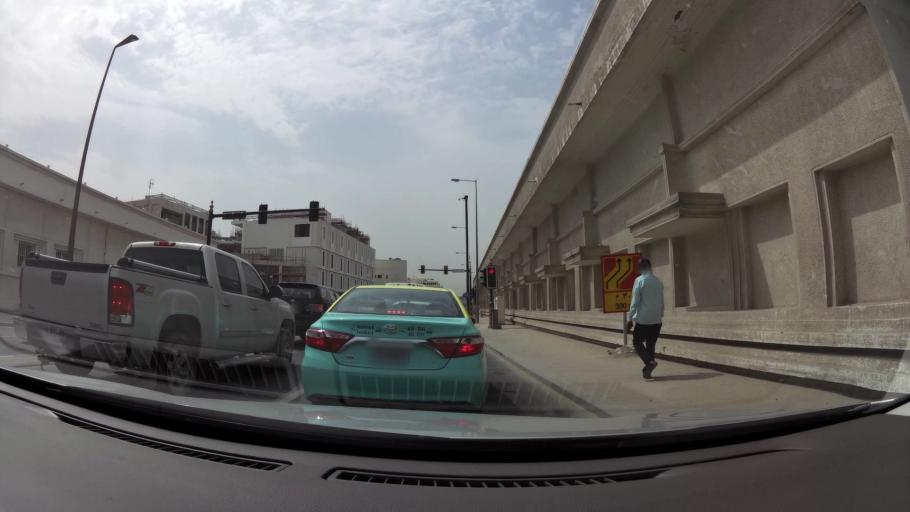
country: QA
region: Baladiyat ad Dawhah
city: Doha
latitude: 25.2885
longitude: 51.5257
